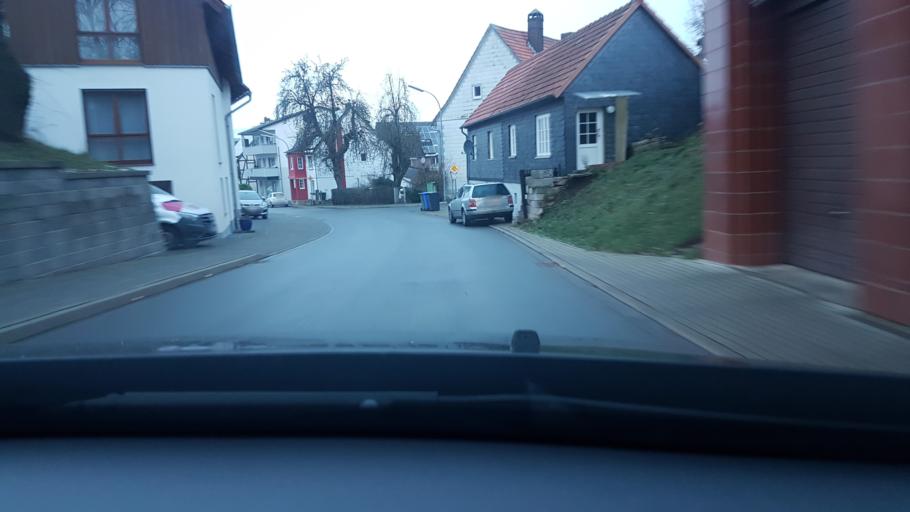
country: DE
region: Hesse
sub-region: Regierungsbezirk Kassel
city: Korbach
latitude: 51.3085
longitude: 8.9088
